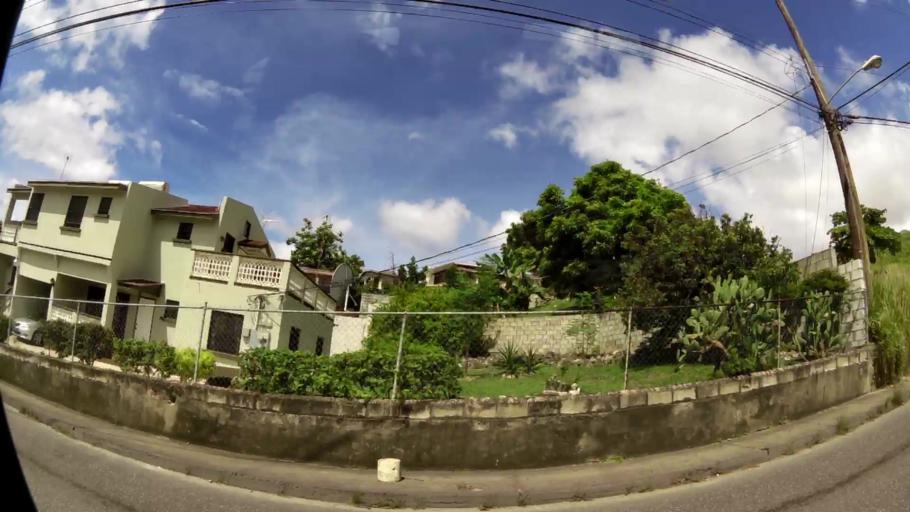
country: BB
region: Saint Michael
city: Bridgetown
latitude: 13.1331
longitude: -59.6234
